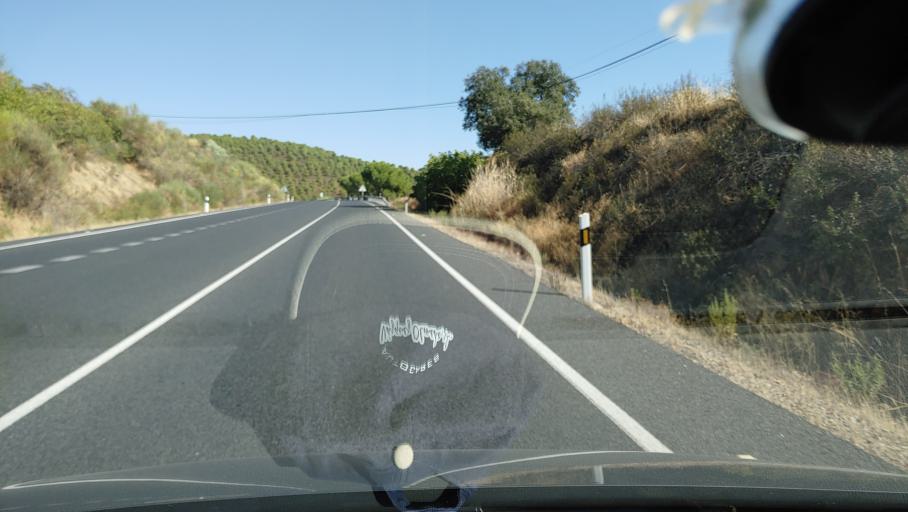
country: ES
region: Andalusia
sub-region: Province of Cordoba
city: Villaharta
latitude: 38.1064
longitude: -4.8793
